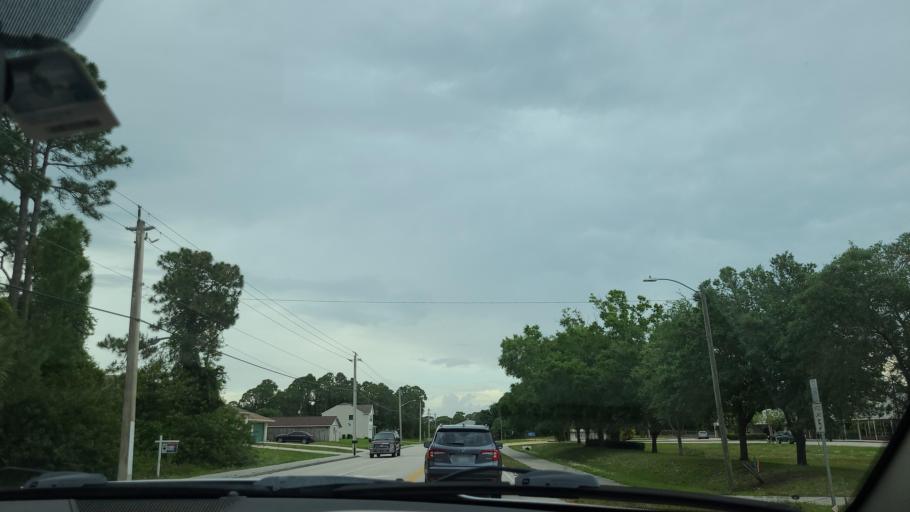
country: US
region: Florida
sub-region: Brevard County
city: West Melbourne
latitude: 27.9898
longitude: -80.6615
